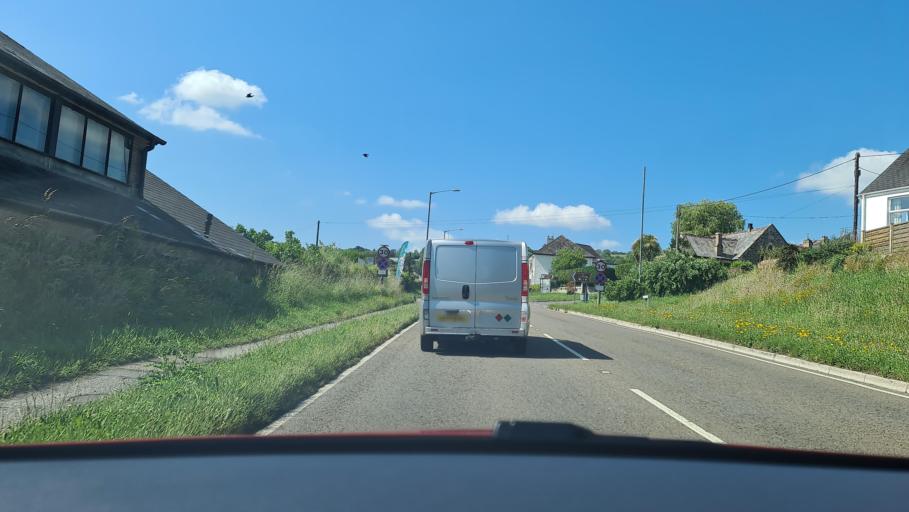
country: GB
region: England
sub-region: Cornwall
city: Lostwithiel
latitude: 50.4092
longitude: -4.6690
